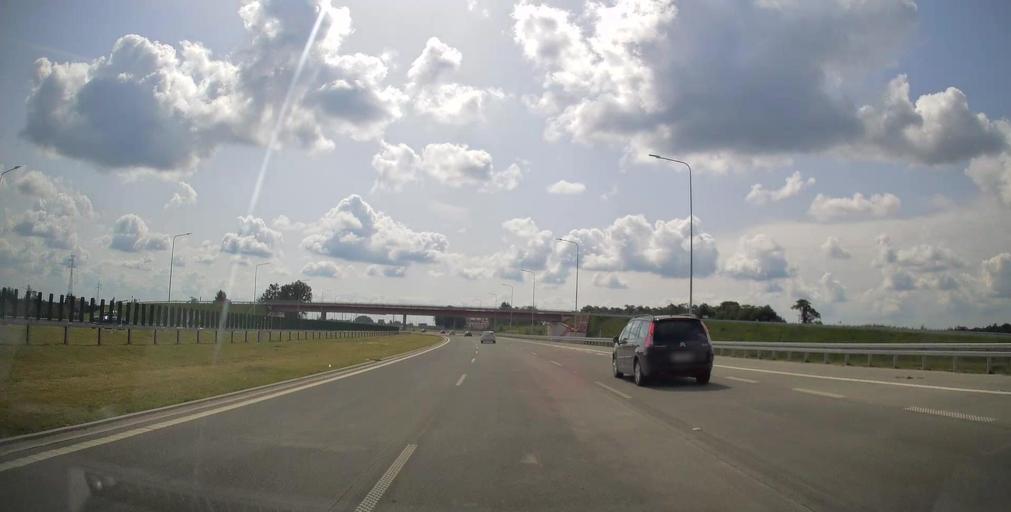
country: PL
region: Masovian Voivodeship
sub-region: Powiat piaseczynski
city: Tarczyn
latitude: 51.9543
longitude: 20.8579
